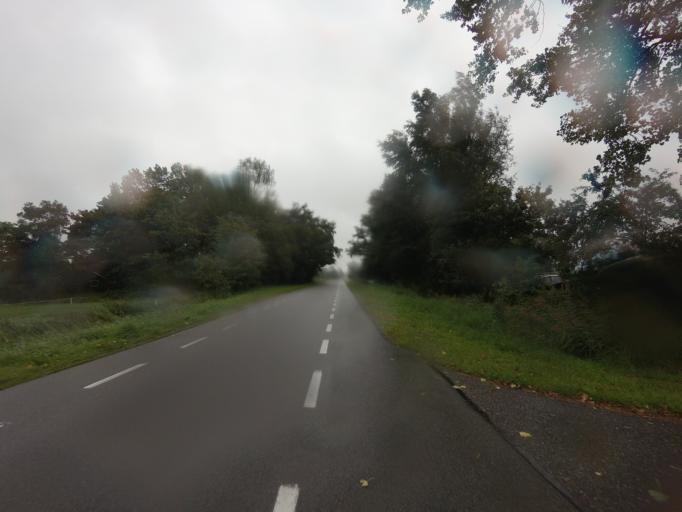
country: NL
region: Friesland
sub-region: Gemeente Smallingerland
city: Oudega
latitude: 53.0965
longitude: 5.9690
